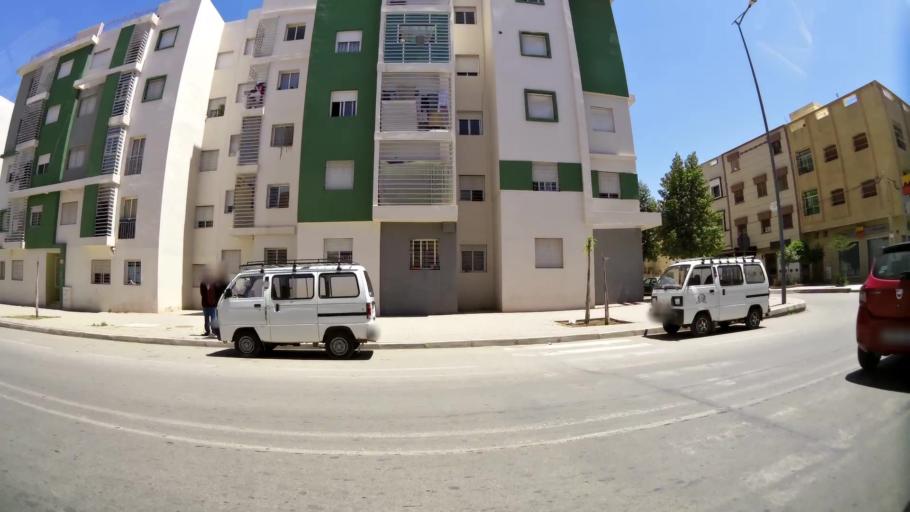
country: MA
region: Oriental
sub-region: Oujda-Angad
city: Oujda
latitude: 34.6610
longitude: -1.9201
